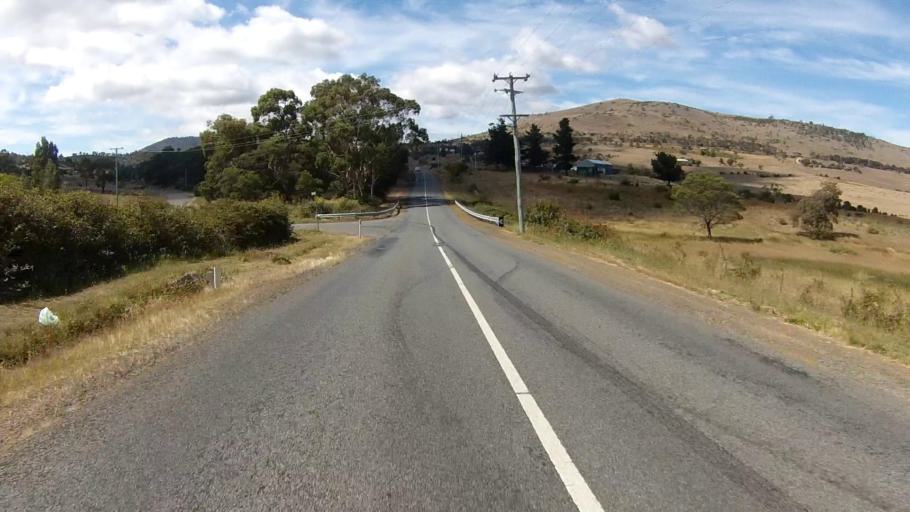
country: AU
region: Tasmania
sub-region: Brighton
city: Bridgewater
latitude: -42.7199
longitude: 147.2790
